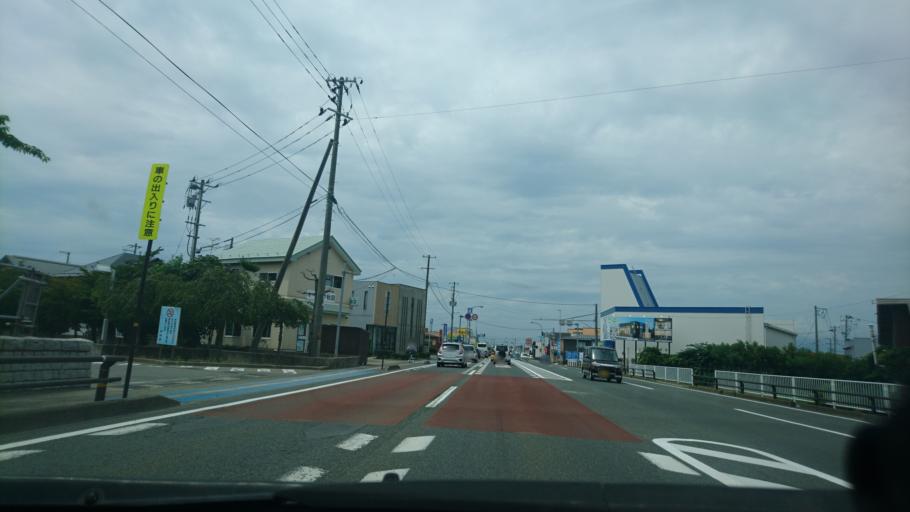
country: JP
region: Akita
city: Akita
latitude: 39.6917
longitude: 140.1221
